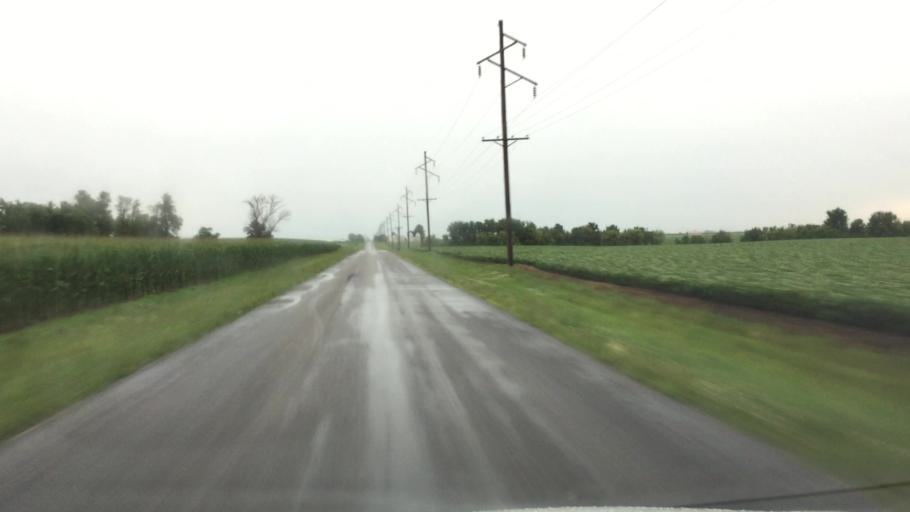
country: US
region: Illinois
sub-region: Hancock County
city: Nauvoo
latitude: 40.5094
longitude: -91.2696
